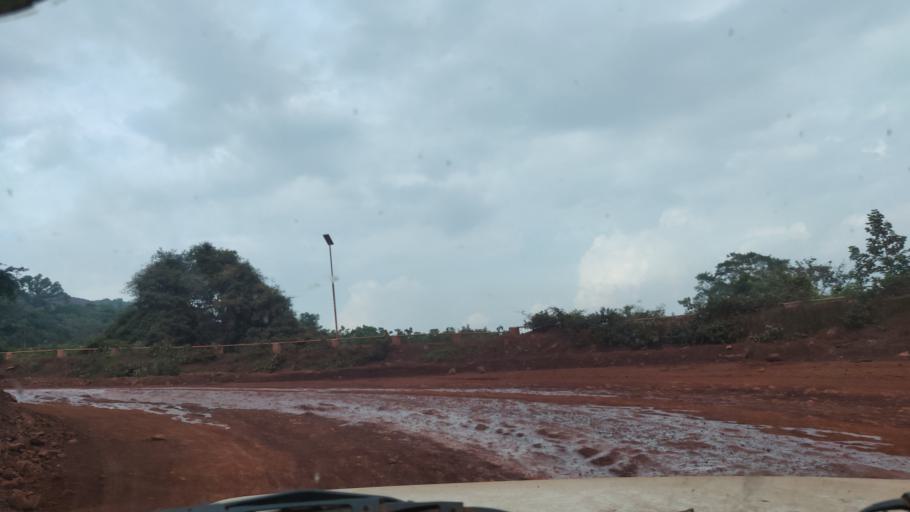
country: IN
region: Odisha
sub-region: Kendujhar
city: Barbil
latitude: 21.6236
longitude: 85.5125
